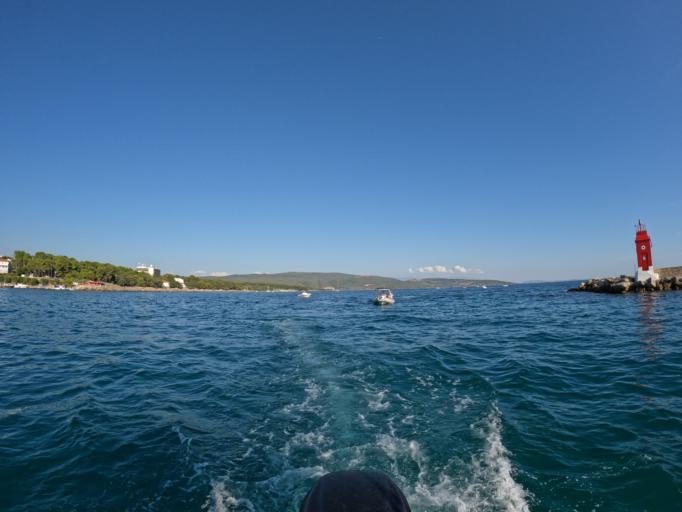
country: HR
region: Primorsko-Goranska
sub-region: Grad Krk
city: Krk
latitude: 45.0243
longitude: 14.5760
